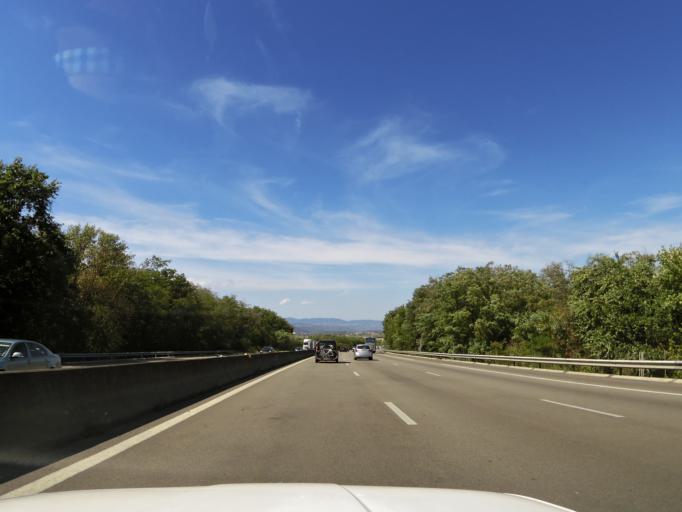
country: FR
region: Rhone-Alpes
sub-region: Departement de la Drome
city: Beausemblant
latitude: 45.2309
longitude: 4.8505
